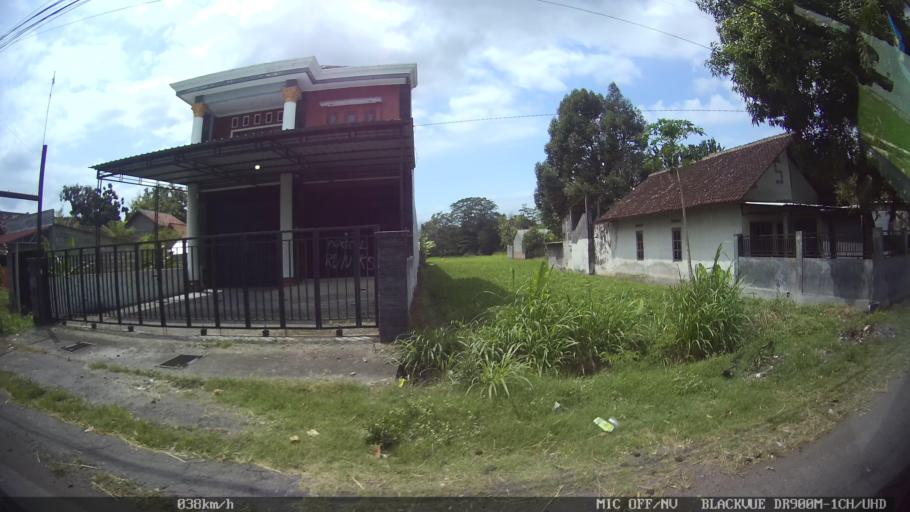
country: ID
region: Daerah Istimewa Yogyakarta
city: Depok
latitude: -7.7982
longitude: 110.4559
